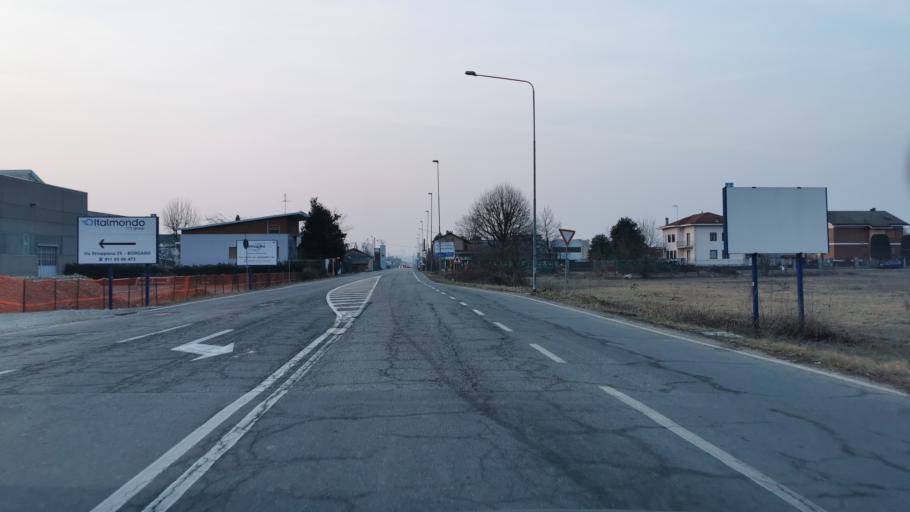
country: IT
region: Piedmont
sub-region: Provincia di Torino
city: Borgaro Torinese
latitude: 45.1448
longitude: 7.6553
